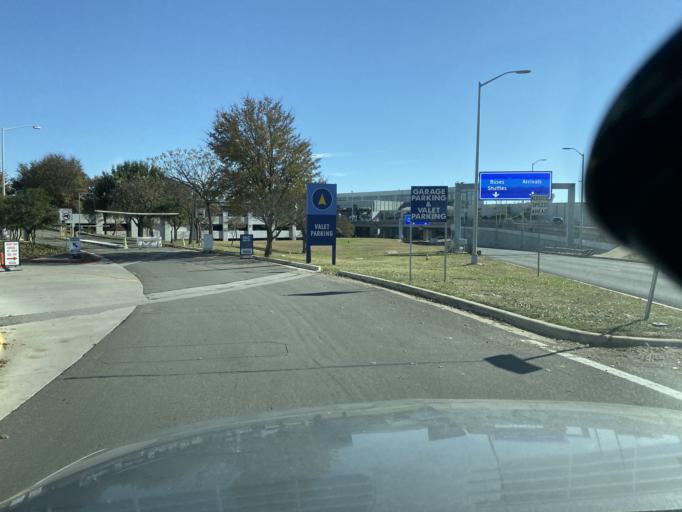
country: US
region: Texas
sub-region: Travis County
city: Austin
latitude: 30.2041
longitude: -97.6700
